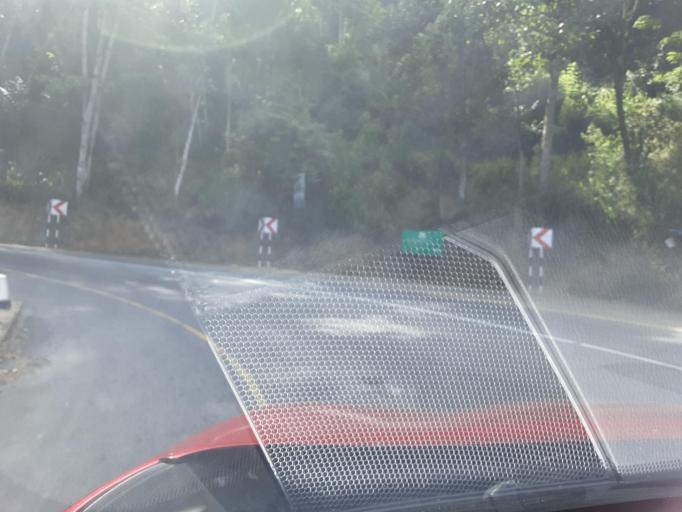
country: LK
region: Uva
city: Badulla
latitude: 6.9842
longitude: 81.0761
